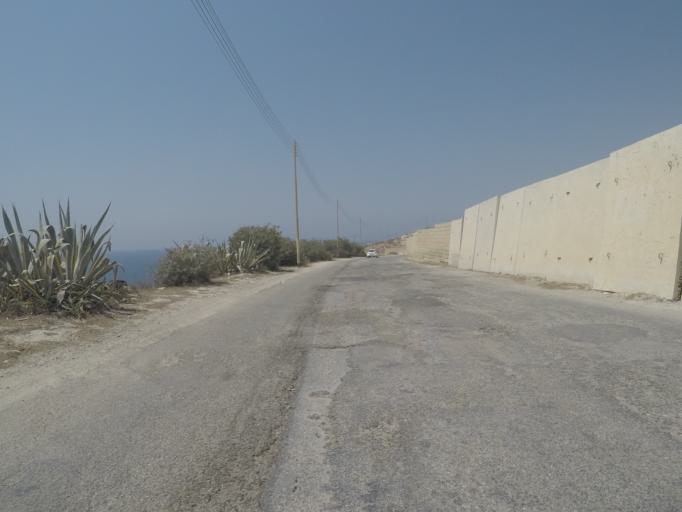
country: MT
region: Is-Siggiewi
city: Siggiewi
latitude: 35.8343
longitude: 14.4186
